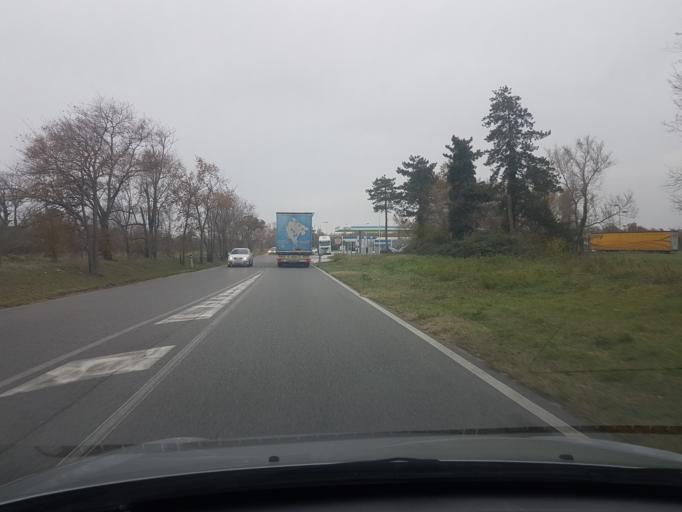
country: IT
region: Friuli Venezia Giulia
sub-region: Provincia di Trieste
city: Prosecco-Contovello
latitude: 45.7079
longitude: 13.7449
